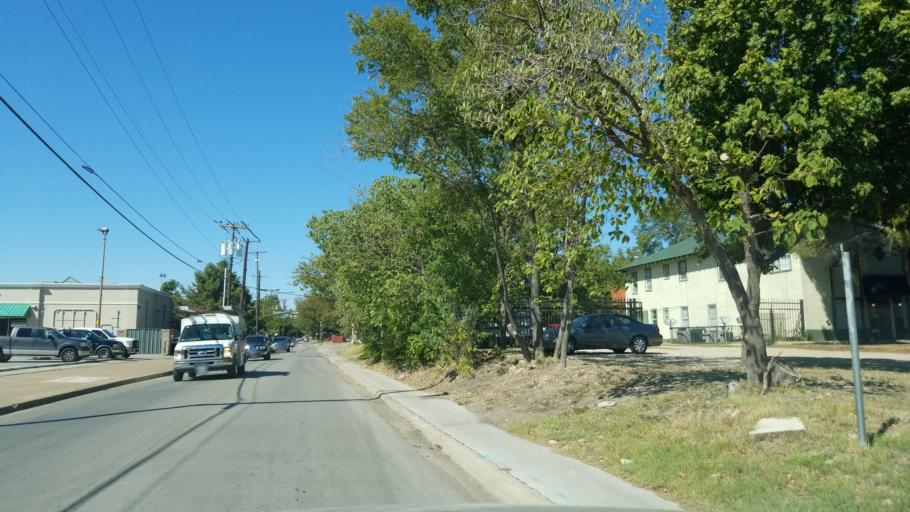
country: US
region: Texas
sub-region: Dallas County
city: Dallas
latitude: 32.7942
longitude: -96.7625
